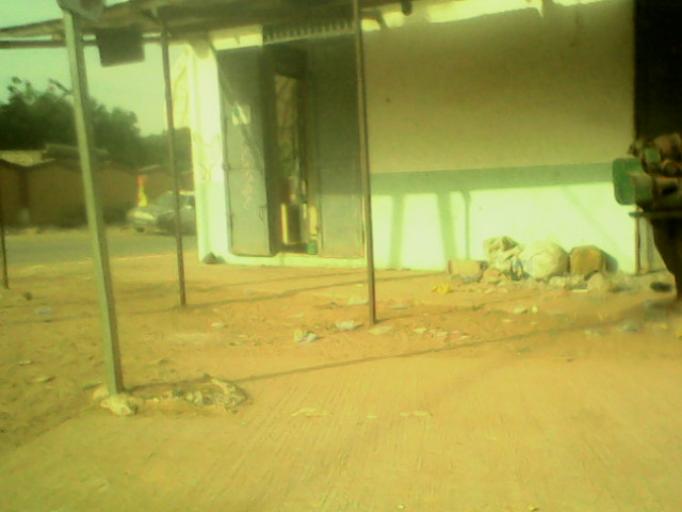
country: SN
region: Diourbel
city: Touba
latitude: 14.8622
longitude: -15.8698
